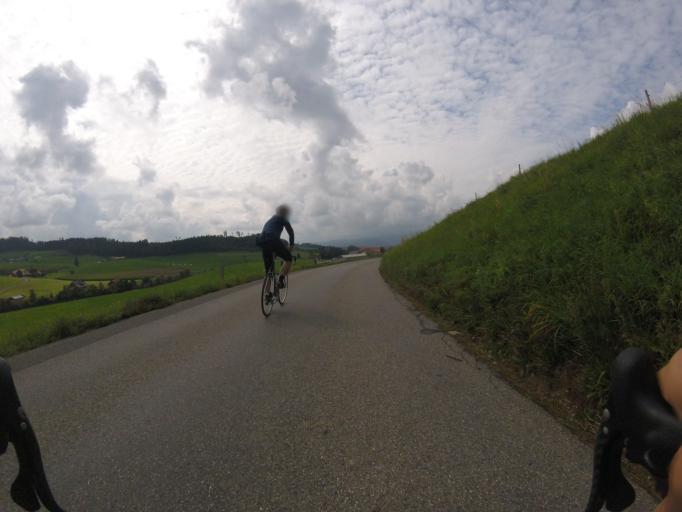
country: CH
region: Bern
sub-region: Bern-Mittelland District
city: Vechigen
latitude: 46.9688
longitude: 7.5750
